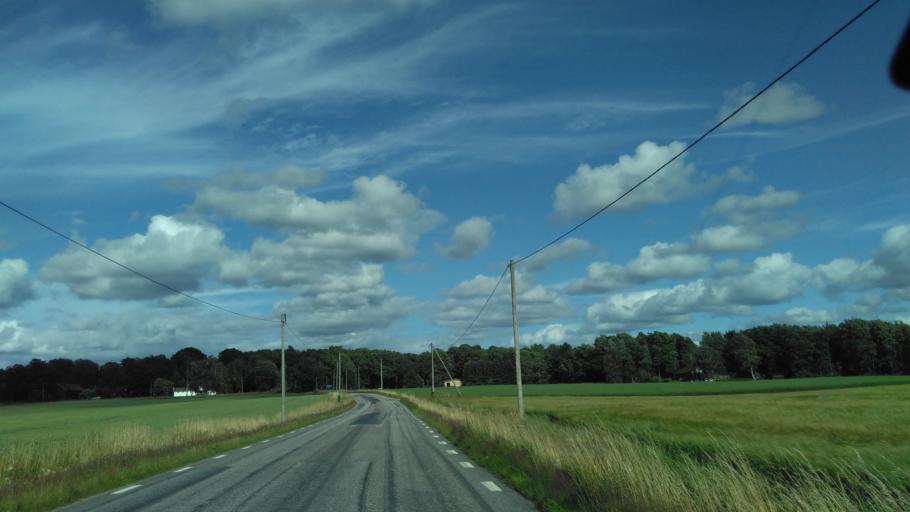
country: SE
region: Vaestra Goetaland
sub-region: Vargarda Kommun
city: Jonstorp
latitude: 58.0131
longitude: 12.6948
